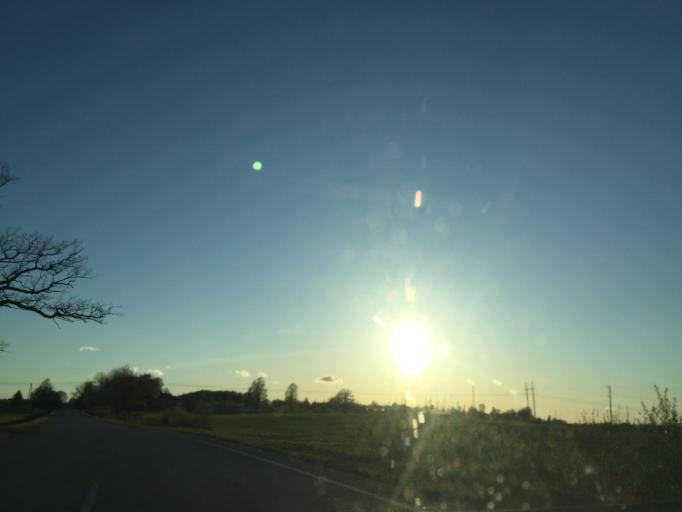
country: LV
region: Skriveri
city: Skriveri
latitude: 56.8854
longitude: 25.2138
